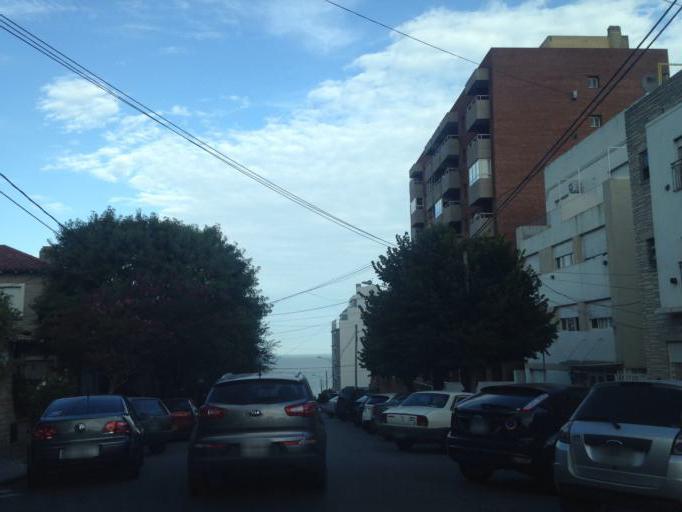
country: AR
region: Buenos Aires
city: Mar del Plata
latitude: -38.0252
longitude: -57.5337
